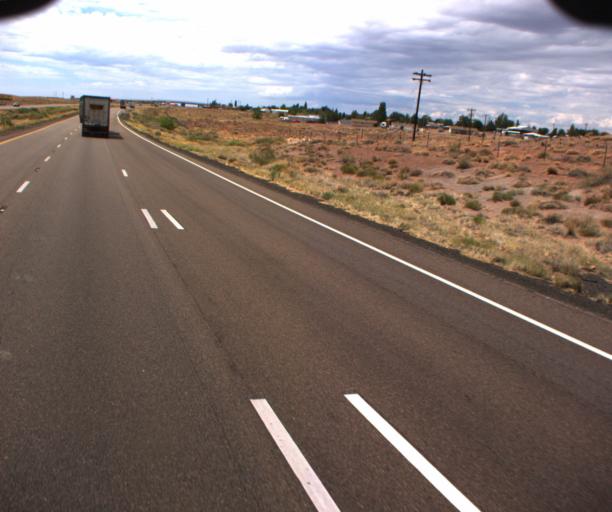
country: US
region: Arizona
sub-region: Navajo County
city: Holbrook
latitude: 34.9331
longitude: -110.1317
